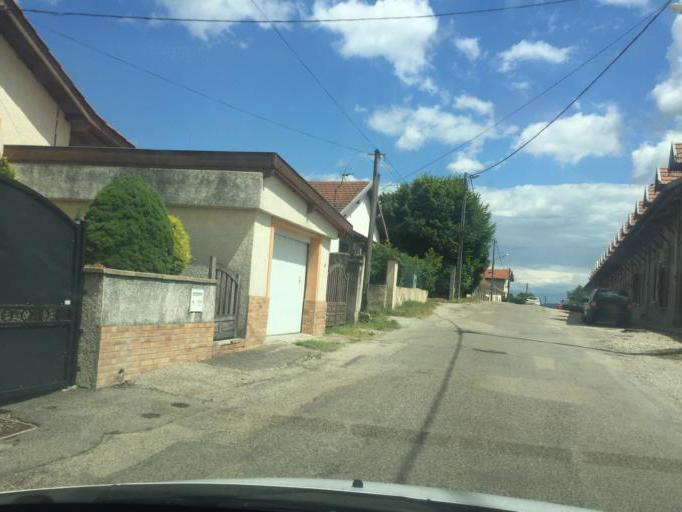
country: FR
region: Rhone-Alpes
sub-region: Departement de l'Isere
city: Charvieu-Chavagneux
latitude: 45.7538
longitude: 5.1615
